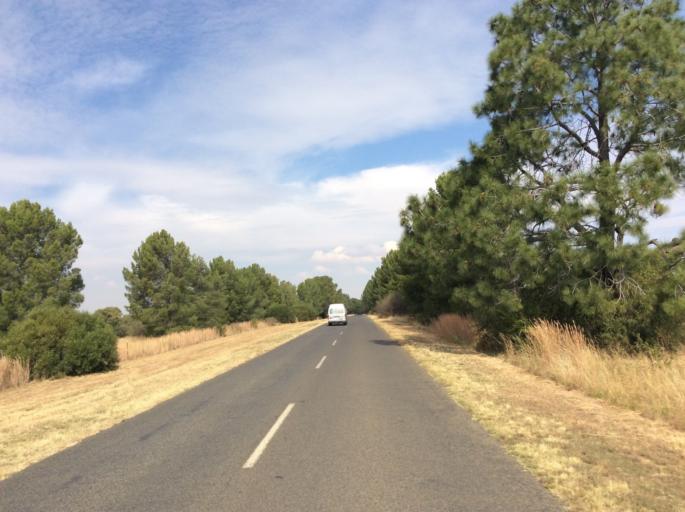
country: ZA
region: Orange Free State
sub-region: Xhariep District Municipality
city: Dewetsdorp
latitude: -29.5664
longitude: 26.6659
